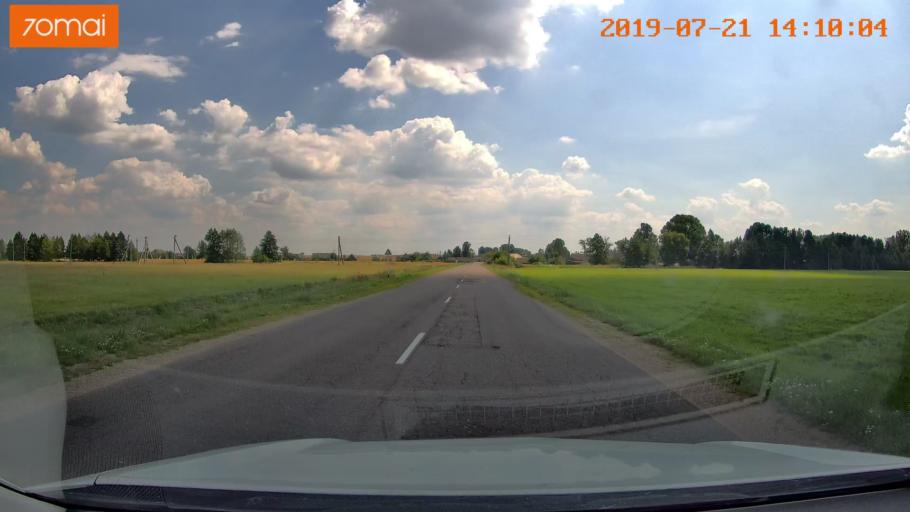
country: BY
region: Grodnenskaya
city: Karelichy
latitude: 53.6664
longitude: 26.1334
